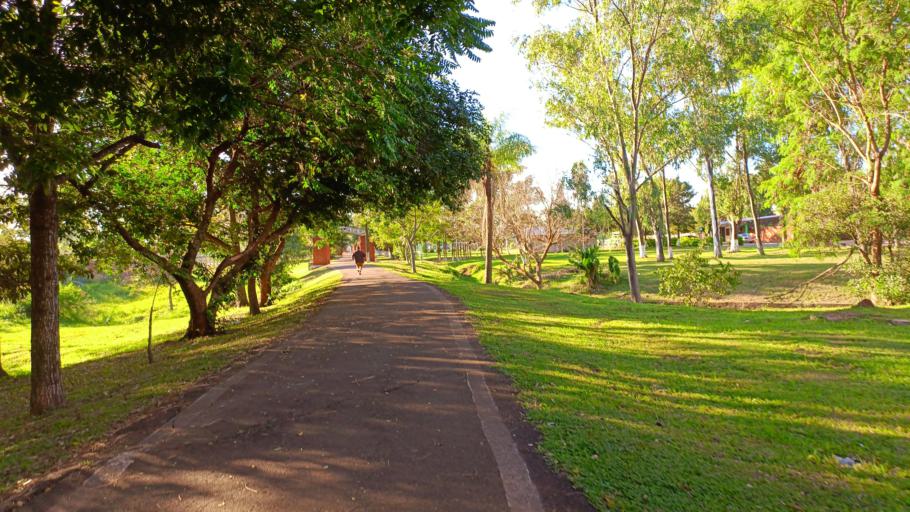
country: PY
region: Itapua
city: Carmen del Parana
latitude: -27.1588
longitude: -56.2404
